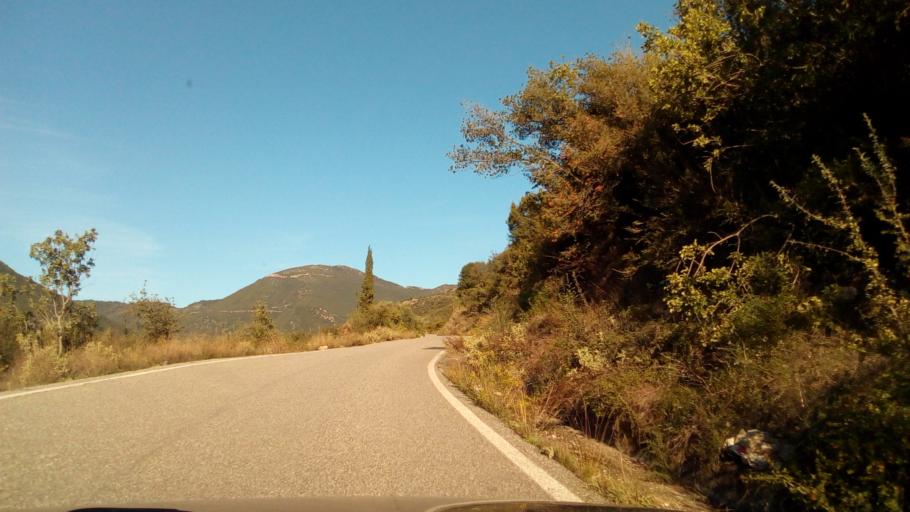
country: GR
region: West Greece
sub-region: Nomos Aitolias kai Akarnanias
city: Nafpaktos
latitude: 38.4742
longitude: 21.8724
